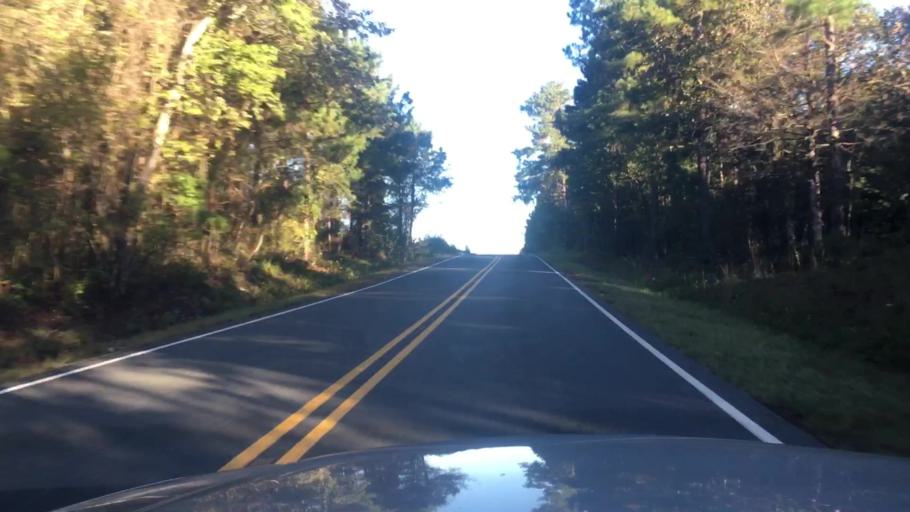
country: US
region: North Carolina
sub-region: Harnett County
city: Walkertown
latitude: 35.2791
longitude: -78.8656
